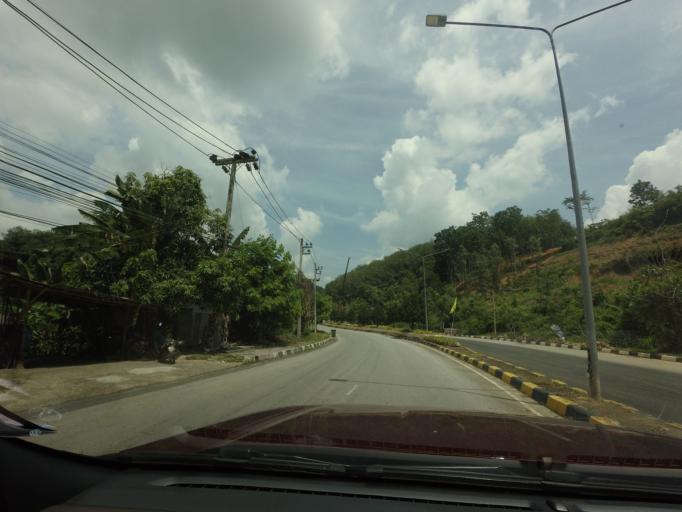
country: TH
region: Yala
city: Betong
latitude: 5.7684
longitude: 101.0582
